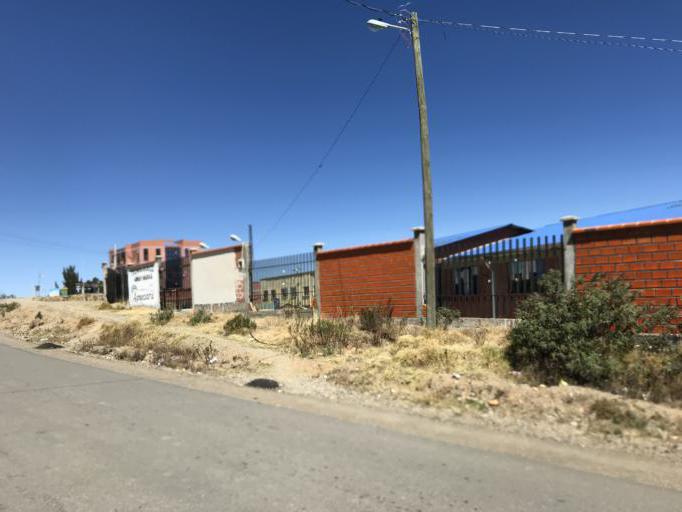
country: BO
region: La Paz
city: Huatajata
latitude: -16.2071
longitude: -68.7006
